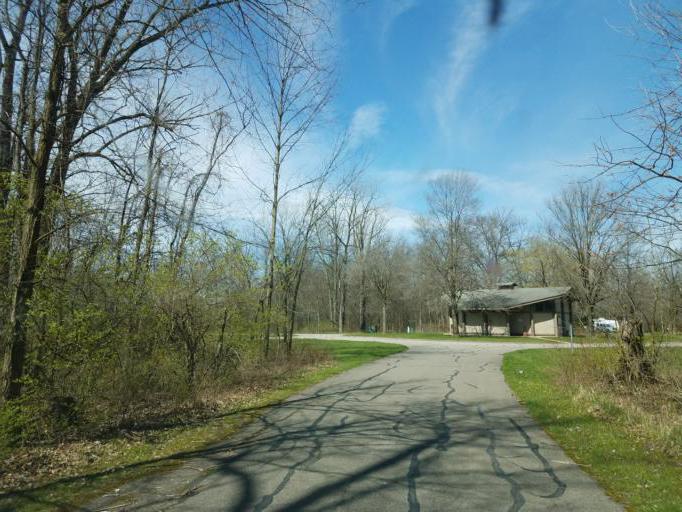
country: US
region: Ohio
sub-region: Delaware County
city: Delaware
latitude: 40.3970
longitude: -83.0594
